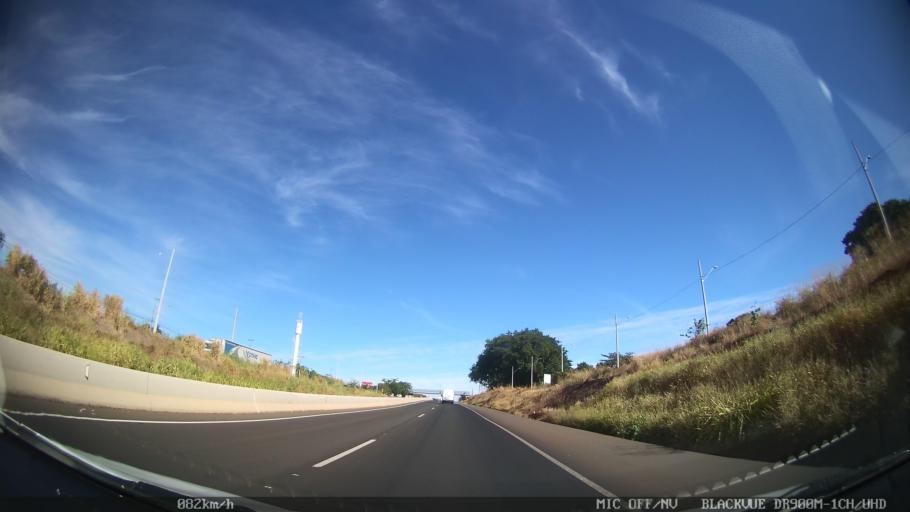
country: BR
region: Sao Paulo
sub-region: Sao Jose Do Rio Preto
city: Sao Jose do Rio Preto
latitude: -20.7891
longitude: -49.3543
